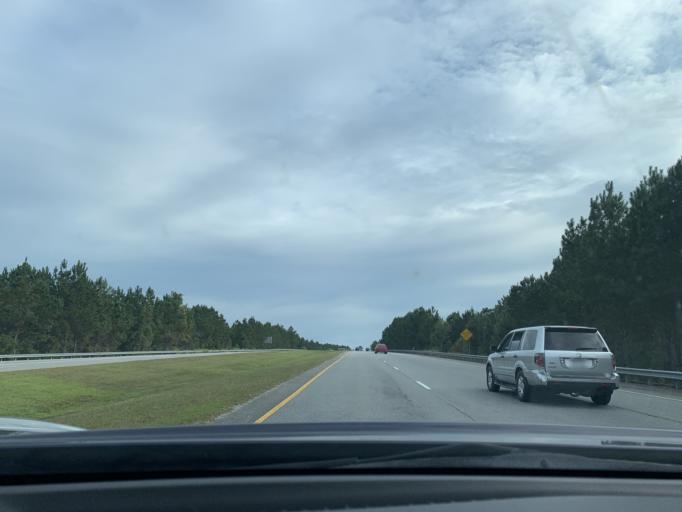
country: US
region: Georgia
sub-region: Chatham County
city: Pooler
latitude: 32.1140
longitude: -81.2682
